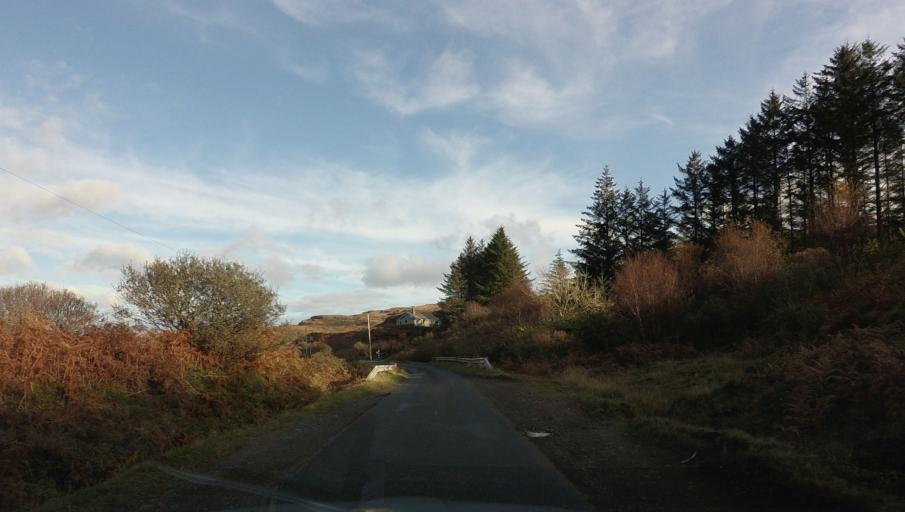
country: GB
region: Scotland
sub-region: Argyll and Bute
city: Isle Of Mull
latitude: 56.3363
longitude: -6.1518
